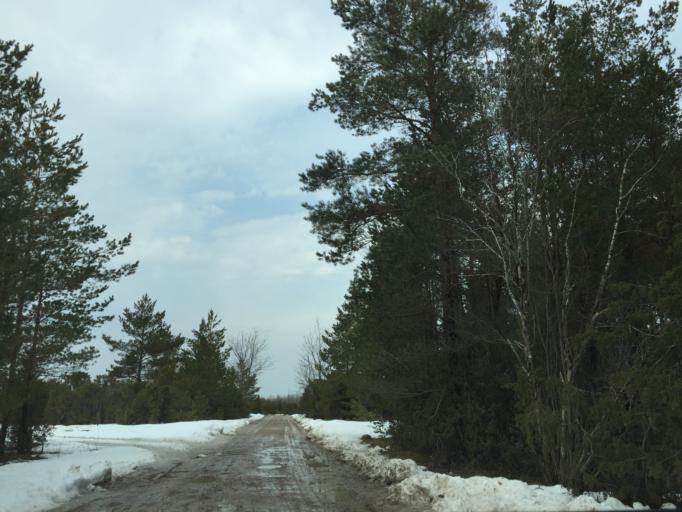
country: EE
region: Saare
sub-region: Kuressaare linn
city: Kuressaare
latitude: 58.4331
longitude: 22.1429
